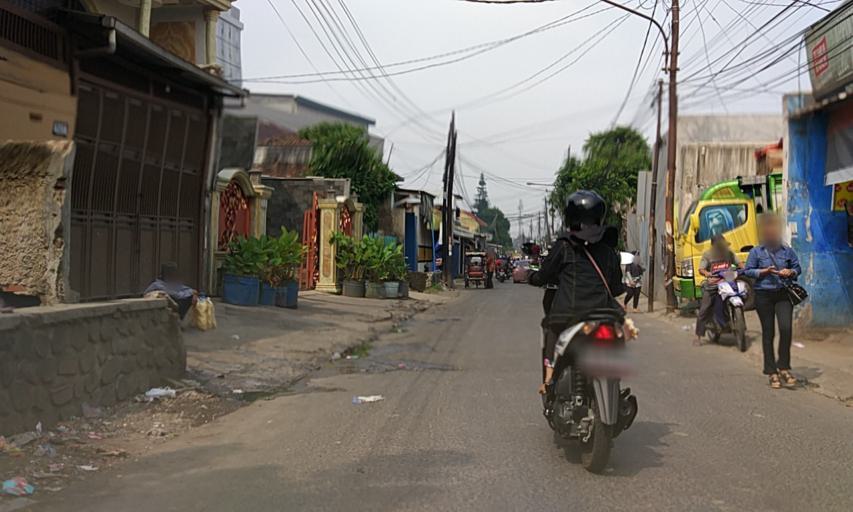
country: ID
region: West Java
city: Bandung
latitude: -6.9280
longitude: 107.5853
